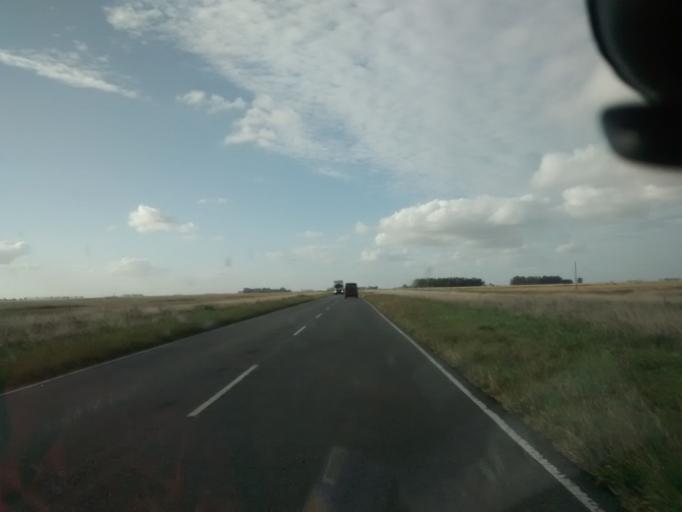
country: AR
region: Buenos Aires
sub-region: Partido de Rauch
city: Rauch
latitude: -36.4810
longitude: -58.5740
